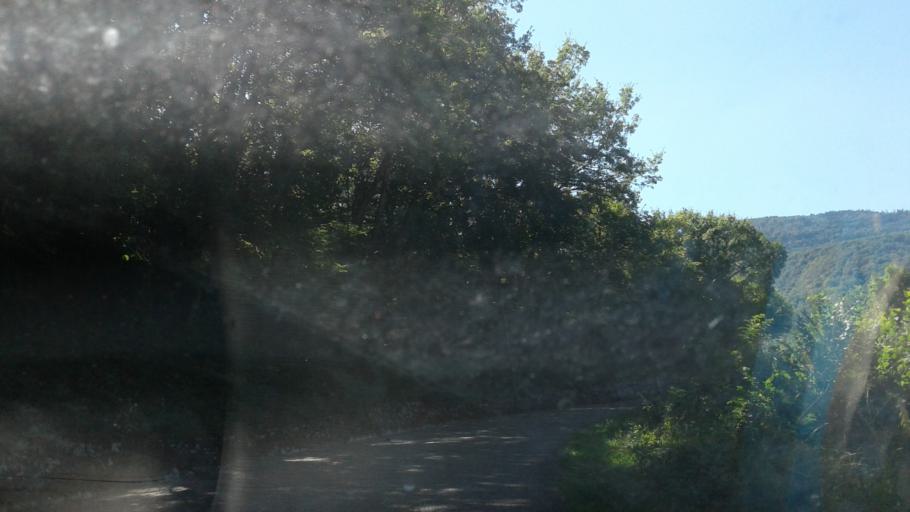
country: FR
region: Rhone-Alpes
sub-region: Departement de l'Ain
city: Artemare
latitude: 45.8746
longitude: 5.6760
